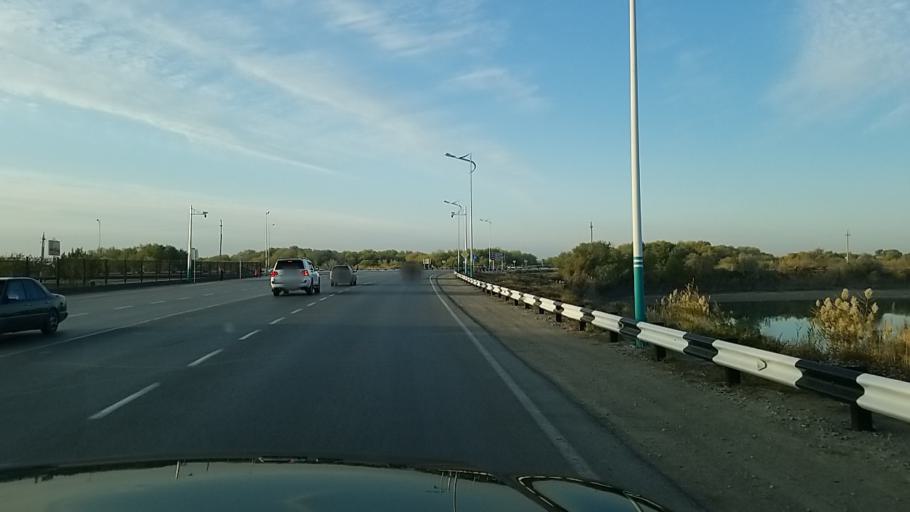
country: KZ
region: Qyzylorda
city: Tasboget
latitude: 44.7753
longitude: 65.5023
